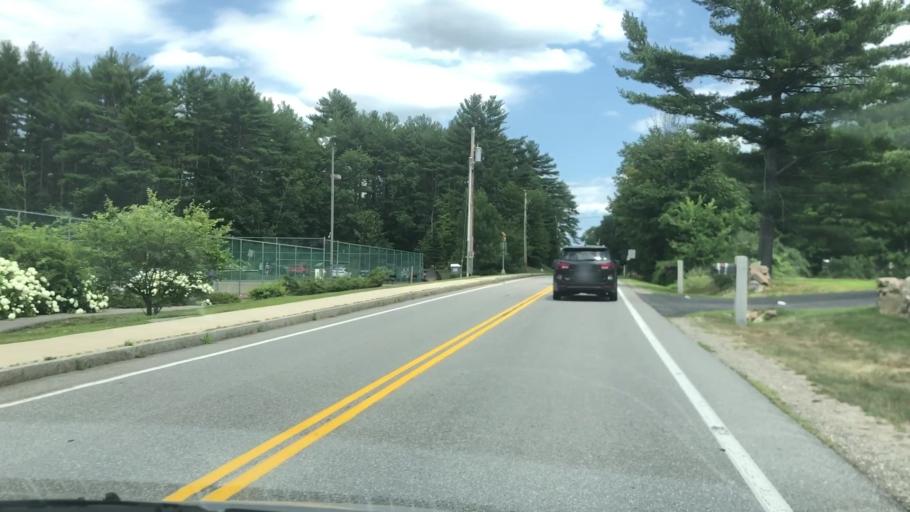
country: US
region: New Hampshire
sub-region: Hillsborough County
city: Bedford
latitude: 42.9368
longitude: -71.5131
